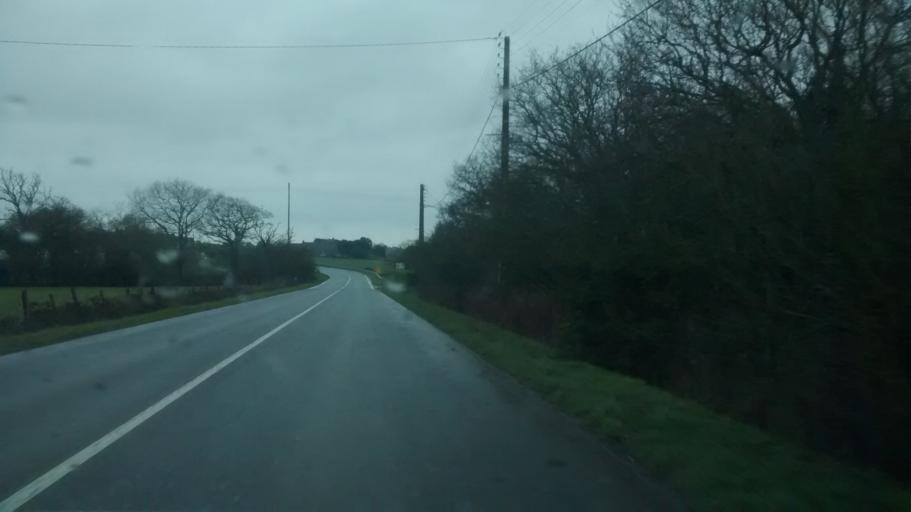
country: FR
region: Brittany
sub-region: Departement d'Ille-et-Vilaine
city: Saint-Coulomb
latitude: 48.6531
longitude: -1.9332
